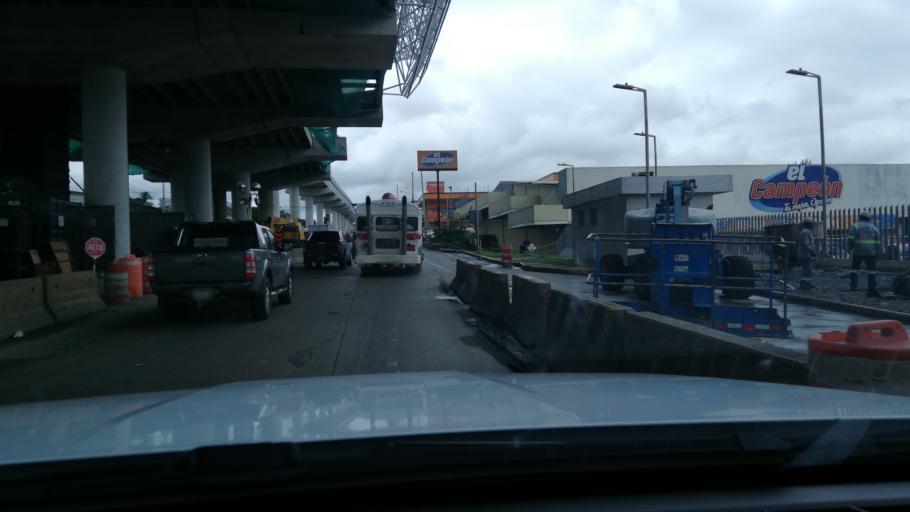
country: PA
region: Panama
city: Tocumen
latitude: 9.1035
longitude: -79.3706
